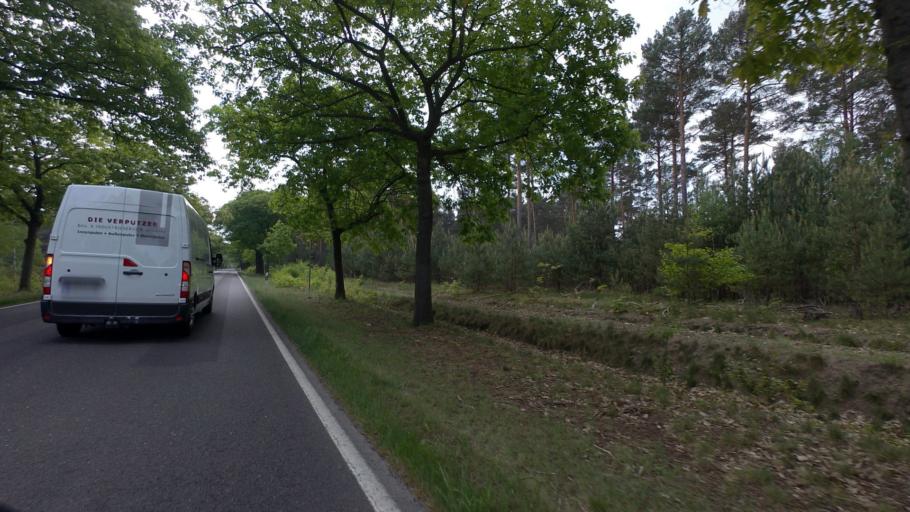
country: DE
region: Brandenburg
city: Drachhausen
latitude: 51.9106
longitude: 14.3523
